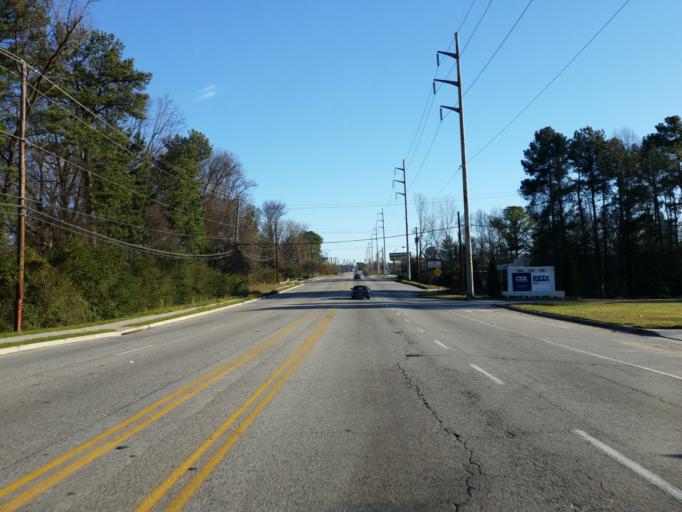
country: US
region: Georgia
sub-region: Fulton County
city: Atlanta
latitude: 33.7967
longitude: -84.4331
